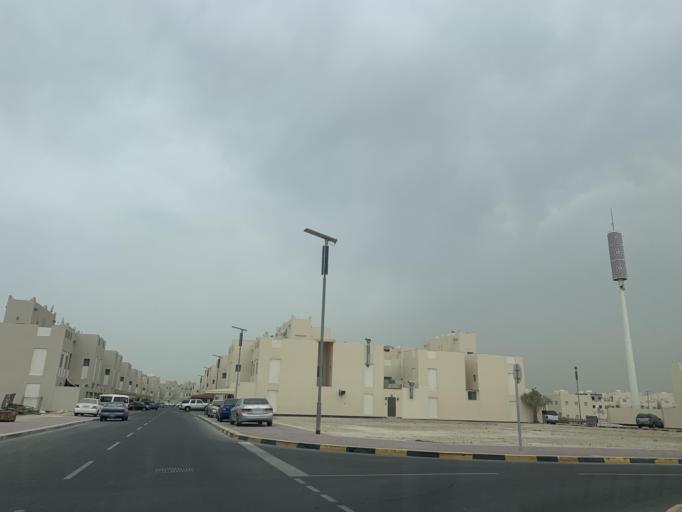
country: BH
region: Northern
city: Madinat `Isa
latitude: 26.1694
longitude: 50.5111
